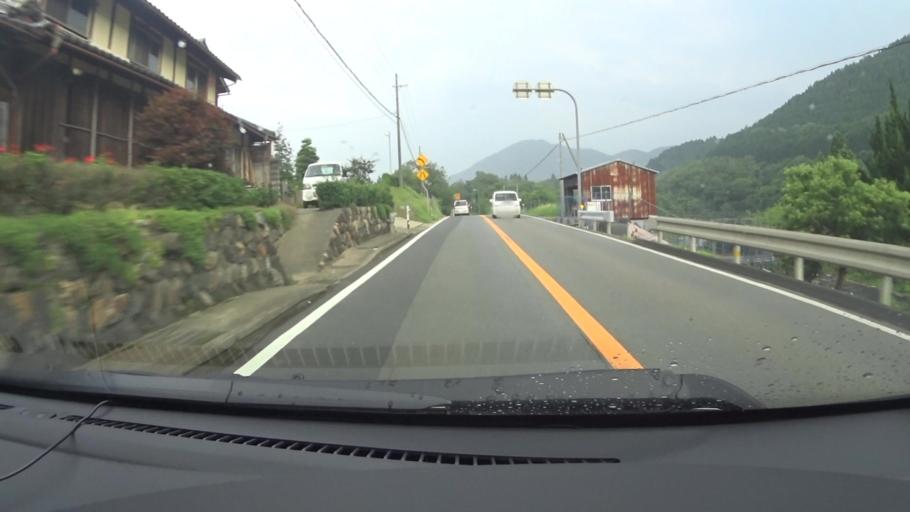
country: JP
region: Kyoto
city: Ayabe
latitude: 35.2295
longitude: 135.4155
